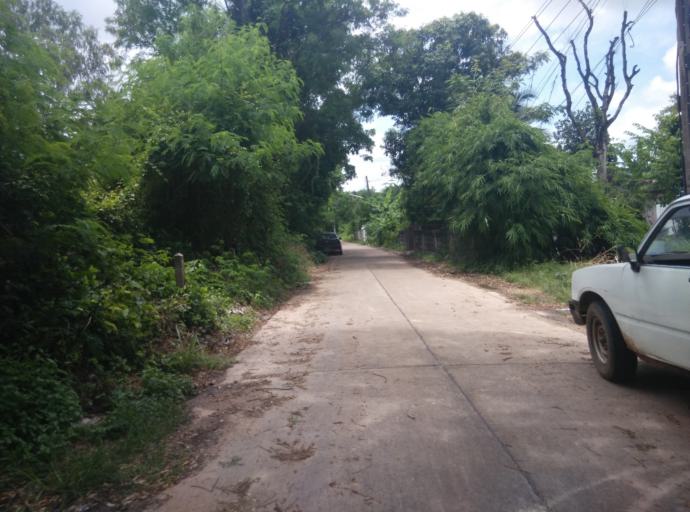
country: TH
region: Sisaket
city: Si Sa Ket
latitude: 15.1085
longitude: 104.3594
